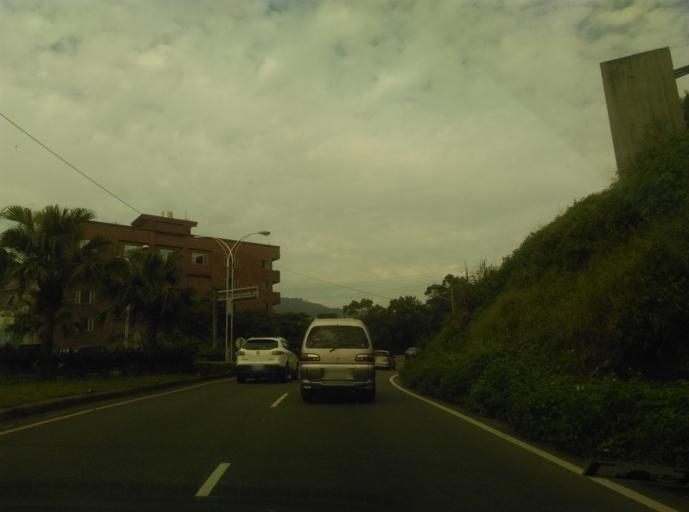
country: TW
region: Taiwan
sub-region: Keelung
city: Keelung
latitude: 25.1557
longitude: 121.6966
